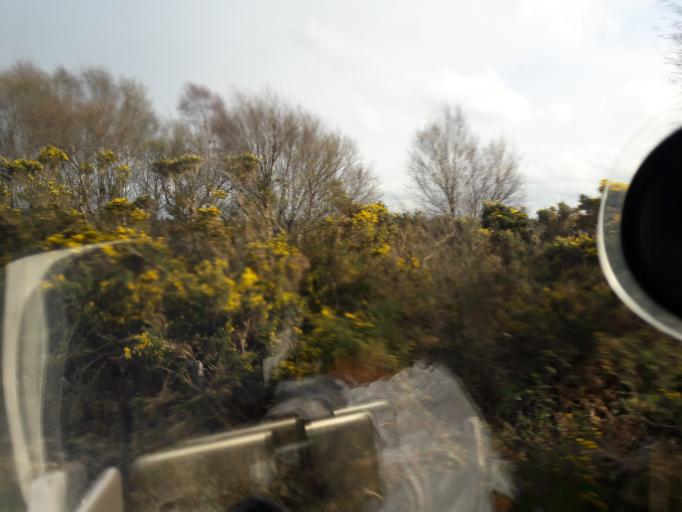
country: IE
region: Leinster
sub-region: An Iarmhi
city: Kinnegad
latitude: 53.4767
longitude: -7.0468
